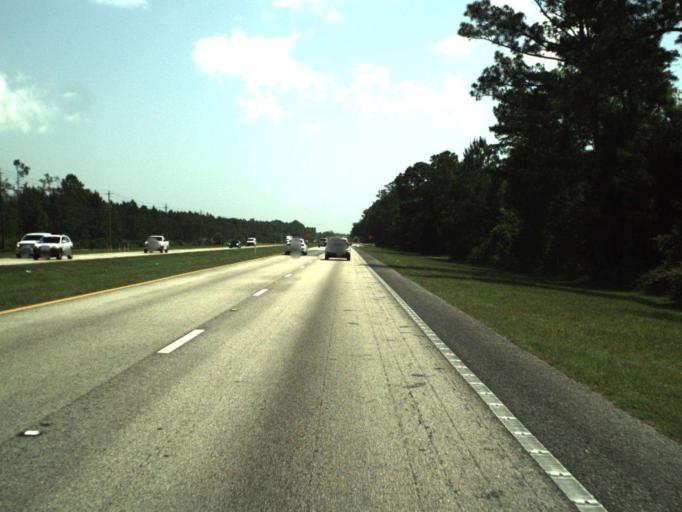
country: US
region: Florida
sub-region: Volusia County
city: Daytona Beach
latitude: 29.1562
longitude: -81.1016
